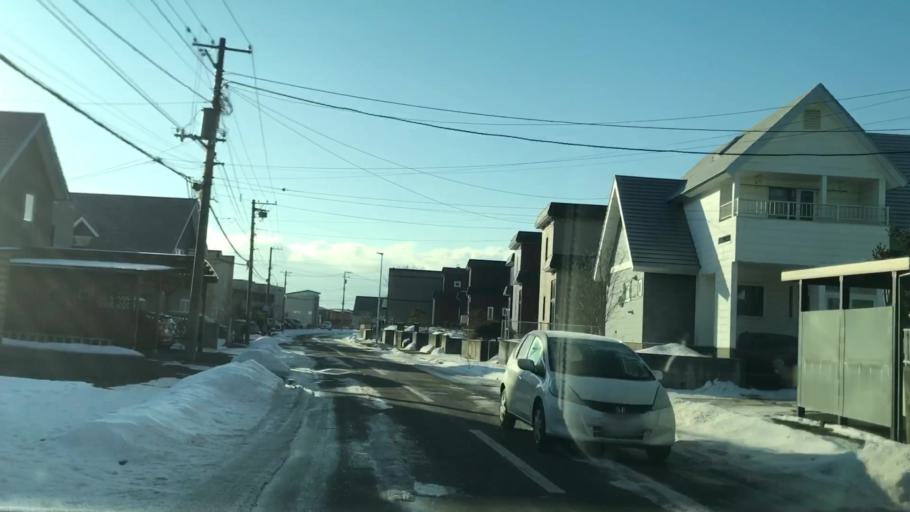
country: JP
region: Hokkaido
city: Muroran
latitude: 42.3868
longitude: 141.0652
